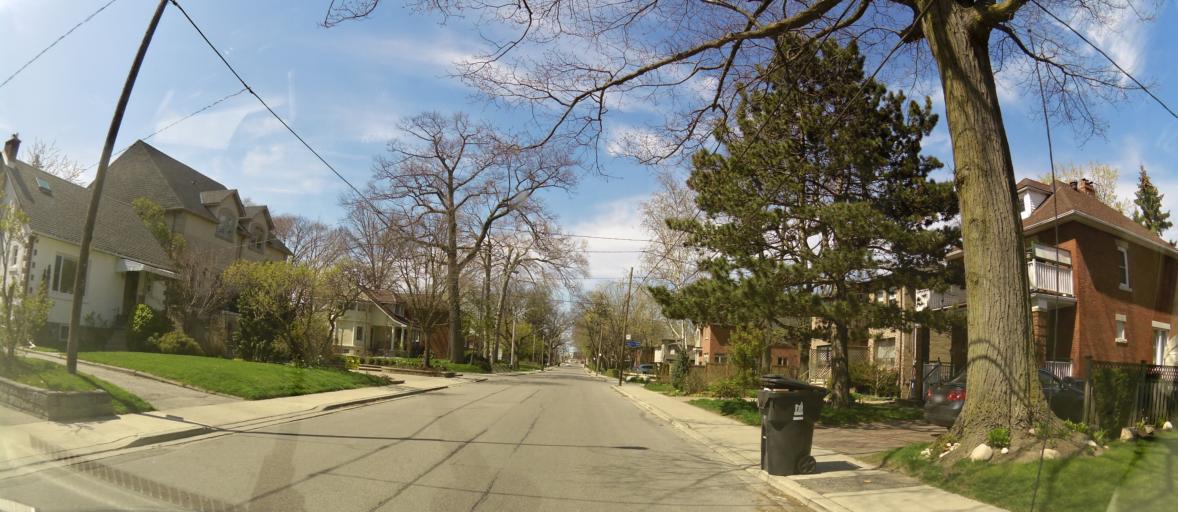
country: CA
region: Ontario
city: Etobicoke
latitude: 43.5910
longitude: -79.5325
